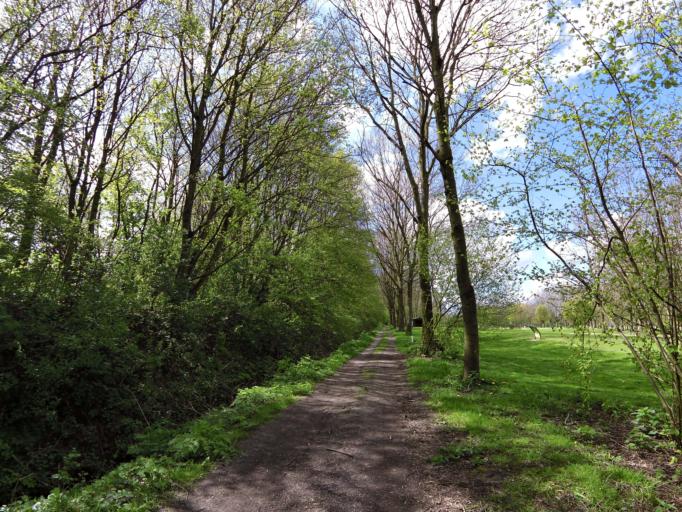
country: NL
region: South Holland
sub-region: Gemeente Binnenmaas
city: Heinenoord
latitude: 51.8373
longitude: 4.4519
